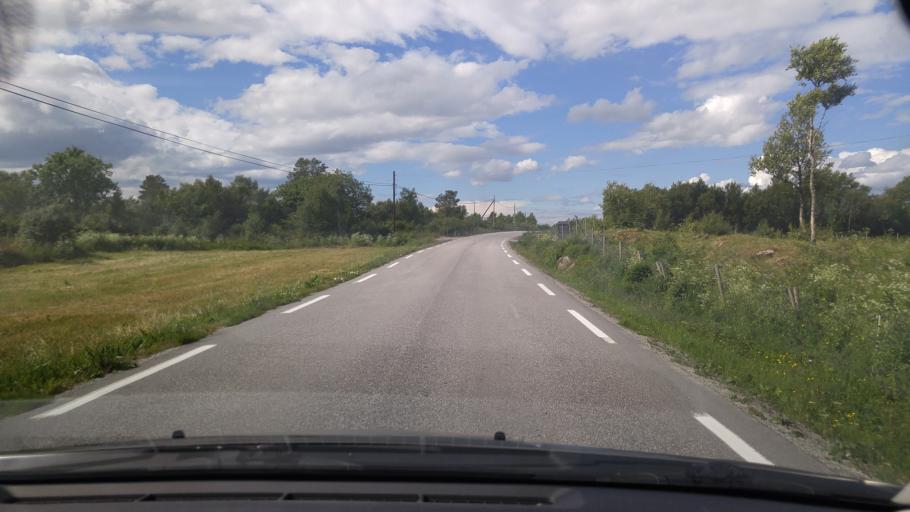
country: NO
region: Nord-Trondelag
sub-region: Vikna
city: Rorvik
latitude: 64.9193
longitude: 11.2237
